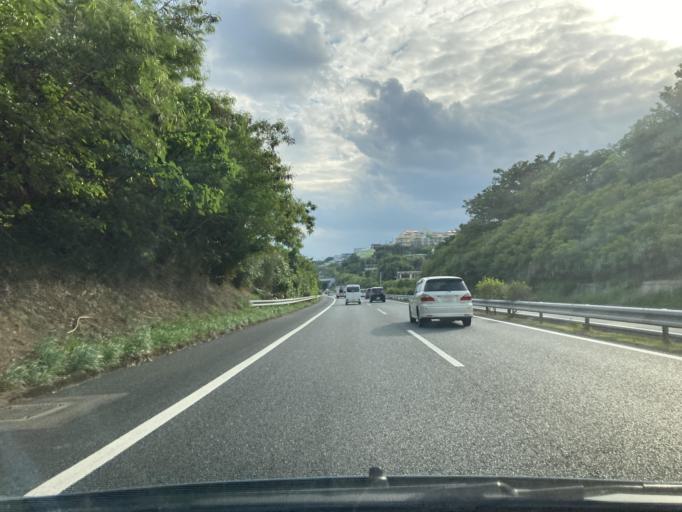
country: JP
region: Okinawa
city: Ginowan
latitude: 26.2717
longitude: 127.7772
